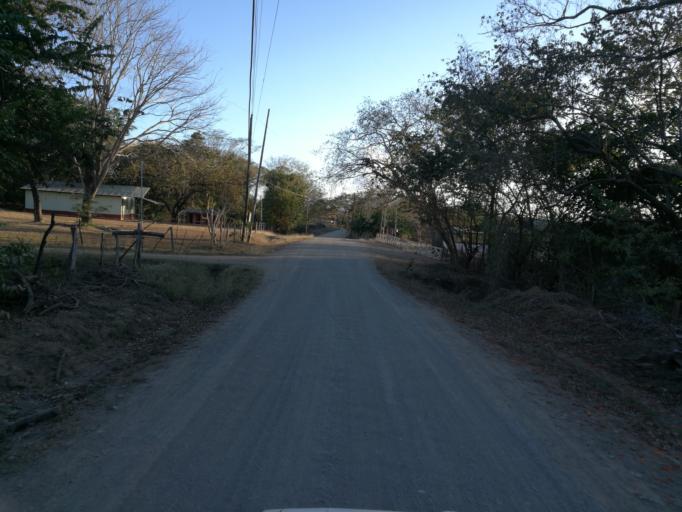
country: CR
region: Guanacaste
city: Nandayure
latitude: 10.1038
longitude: -85.1826
